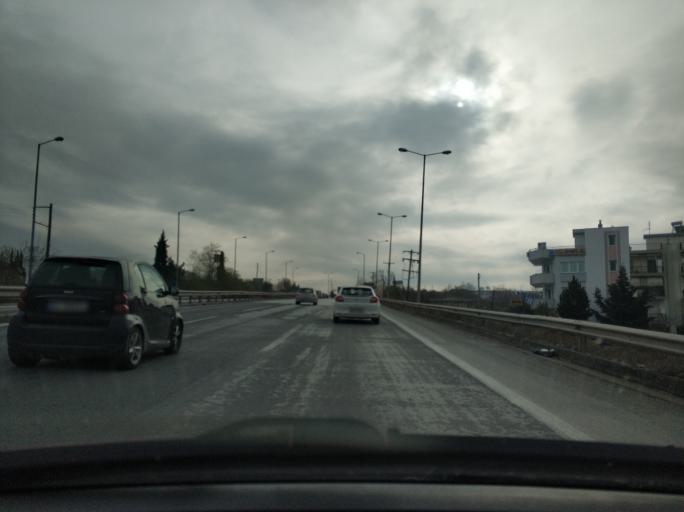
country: GR
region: Central Macedonia
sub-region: Nomos Thessalonikis
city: Pylaia
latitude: 40.5881
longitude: 22.9697
